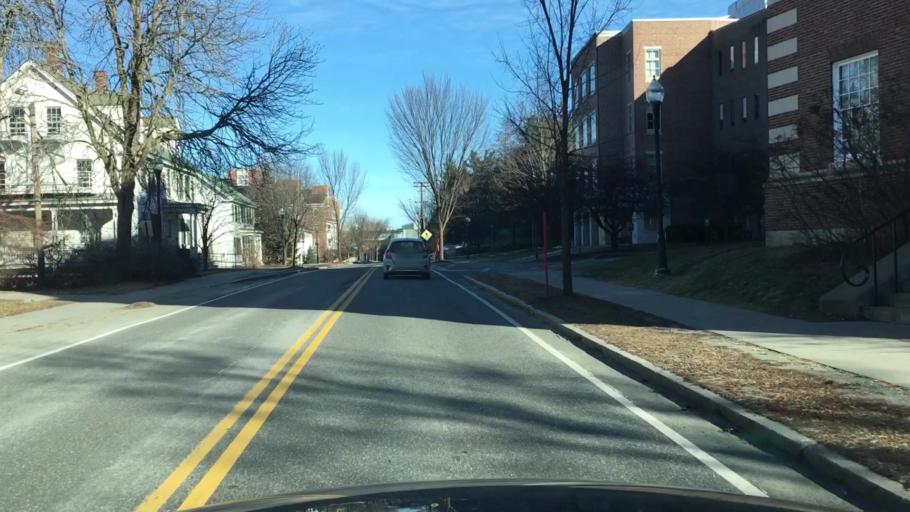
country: US
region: New Hampshire
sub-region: Grafton County
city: Hanover
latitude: 43.7058
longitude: -72.2872
